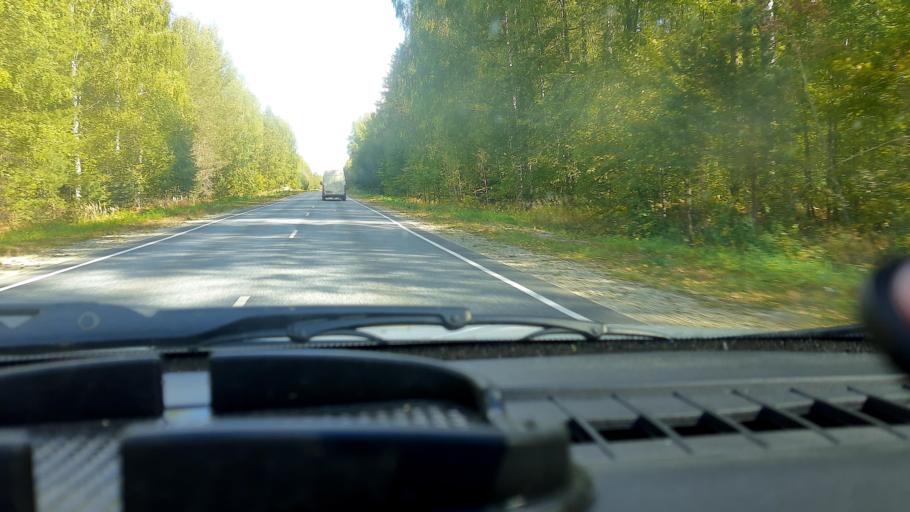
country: RU
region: Kirov
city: Sanchursk
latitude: 56.5758
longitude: 47.1893
